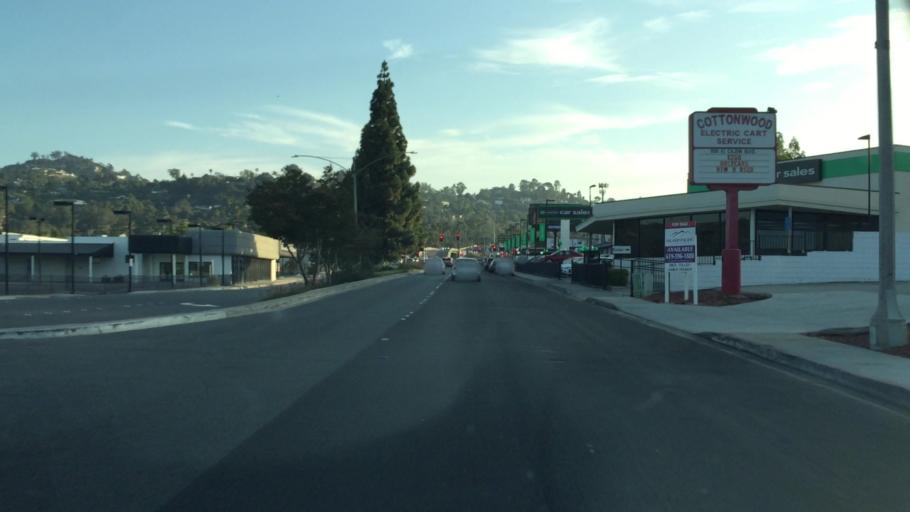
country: US
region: California
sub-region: San Diego County
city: El Cajon
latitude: 32.7861
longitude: -116.9766
